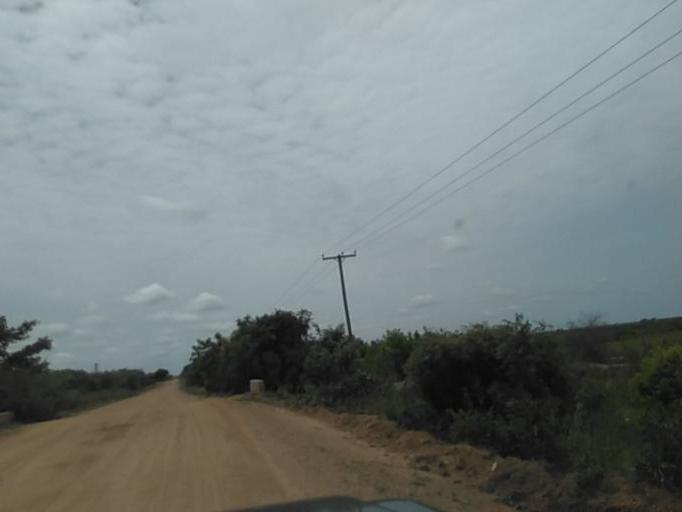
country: GH
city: Akropong
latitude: 6.0401
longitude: 0.2998
